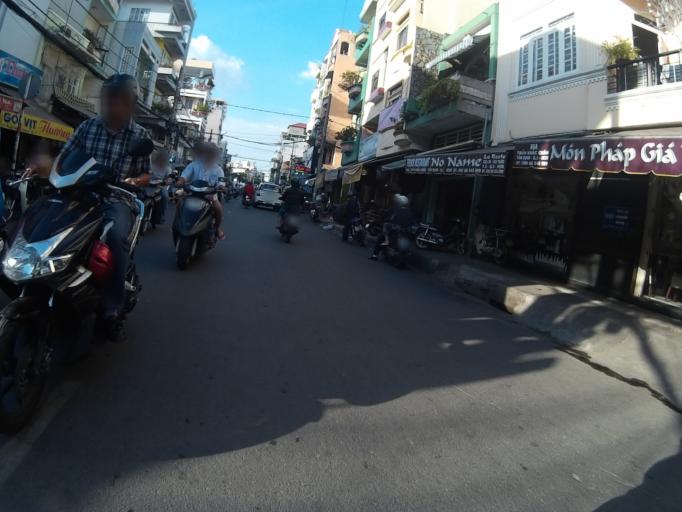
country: VN
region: Ho Chi Minh City
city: Quan Binh Thanh
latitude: 10.7944
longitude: 106.6909
